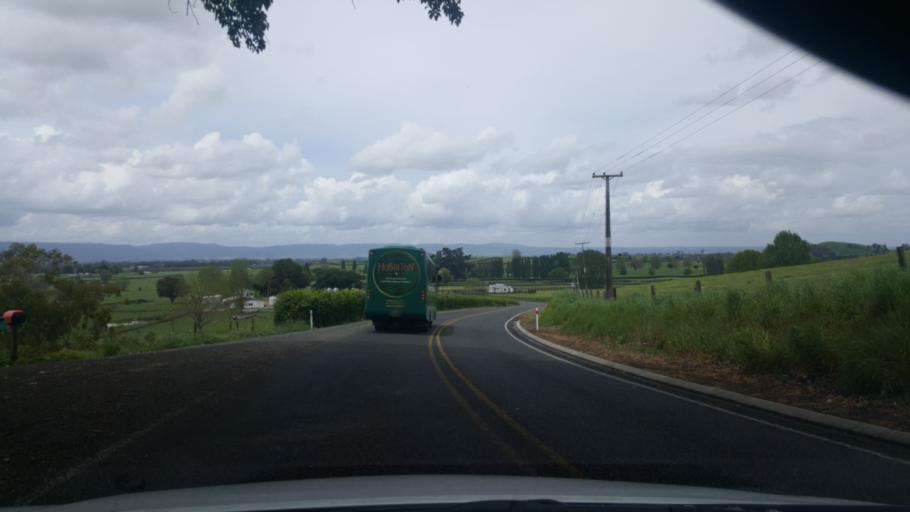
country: NZ
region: Waikato
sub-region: Matamata-Piako District
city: Matamata
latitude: -37.8767
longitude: 175.7011
